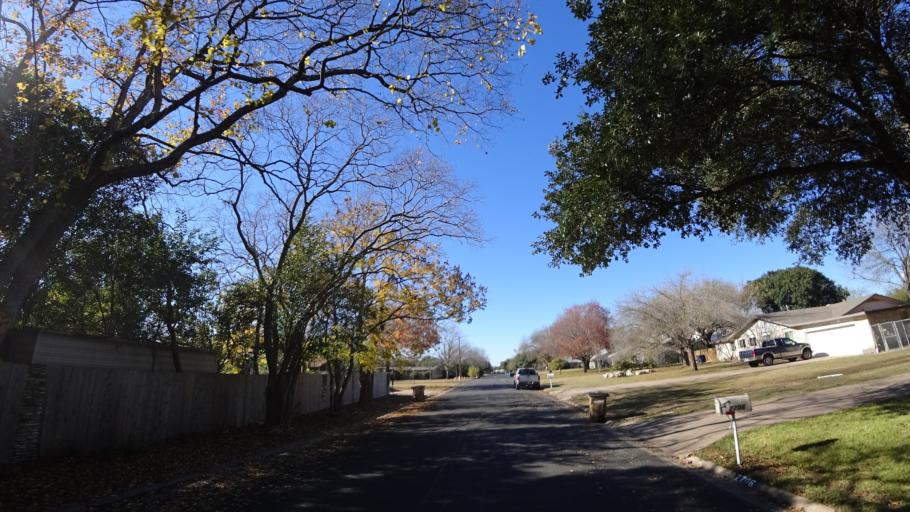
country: US
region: Texas
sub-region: Travis County
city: Wells Branch
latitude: 30.4206
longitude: -97.6966
